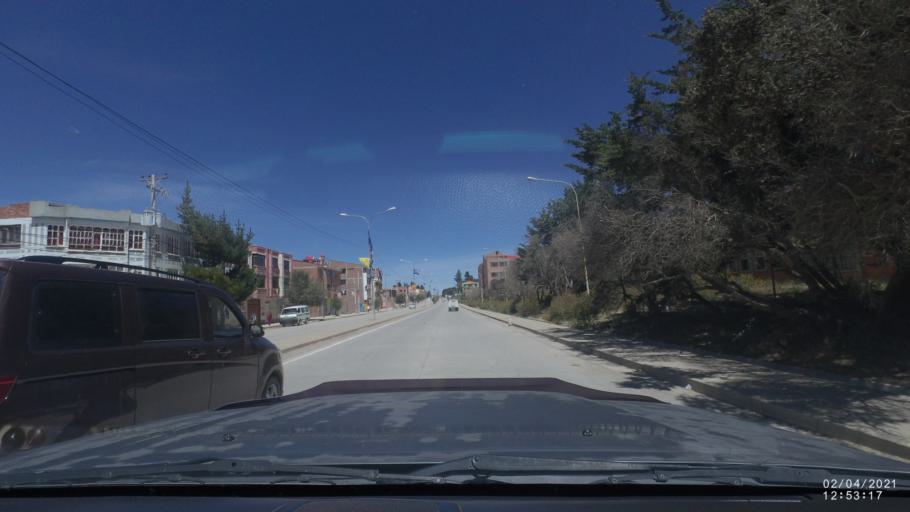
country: BO
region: Oruro
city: Oruro
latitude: -17.9905
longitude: -67.1352
